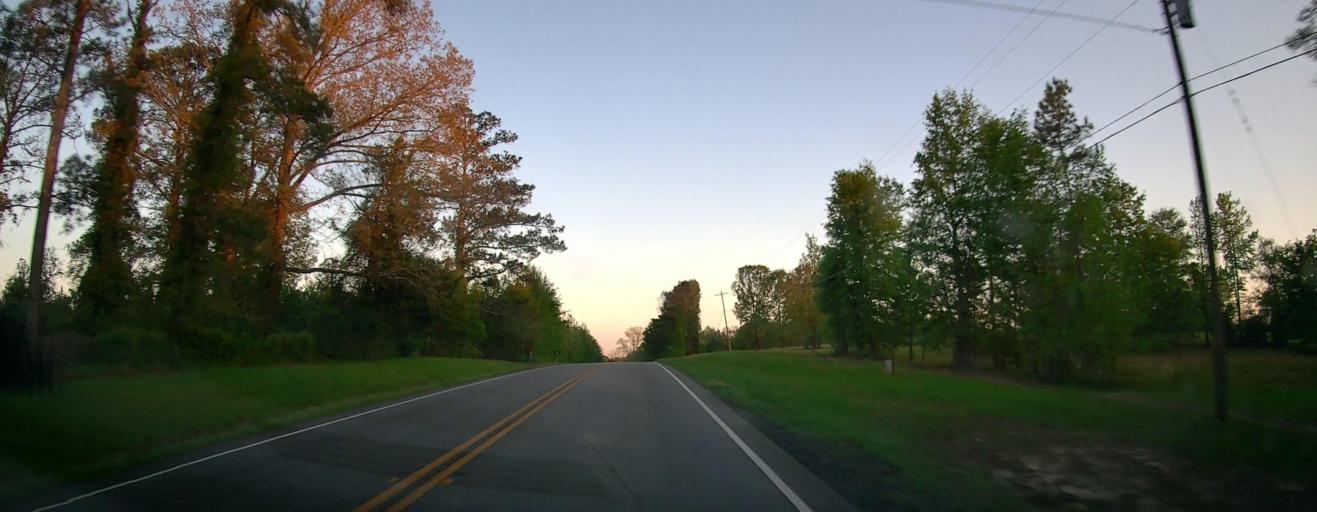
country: US
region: Georgia
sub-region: Marion County
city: Buena Vista
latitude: 32.3579
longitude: -84.5382
